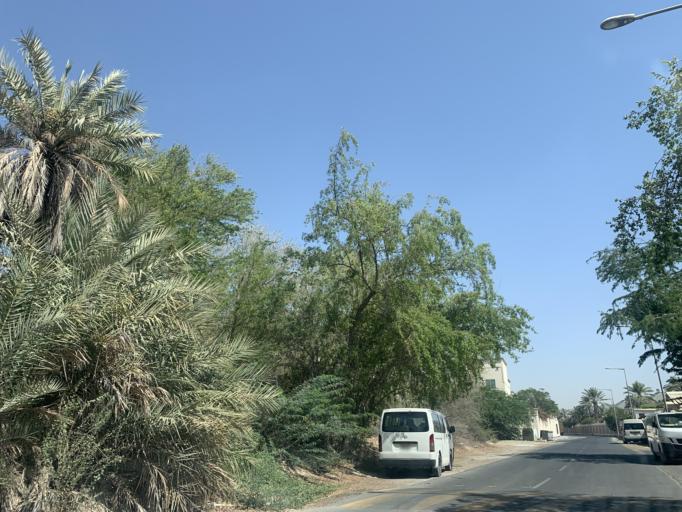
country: BH
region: Manama
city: Jidd Hafs
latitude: 26.2255
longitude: 50.4992
